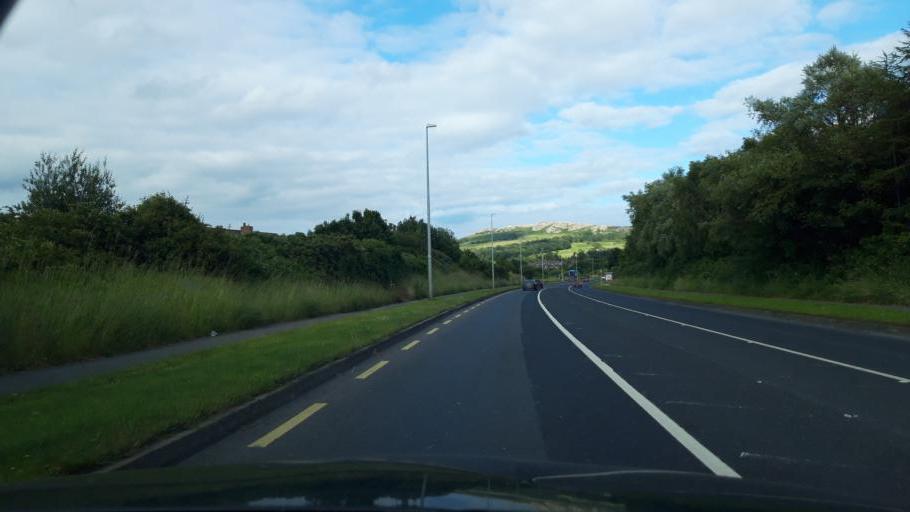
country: IE
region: Leinster
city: Little Bray
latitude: 53.1837
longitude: -6.1203
